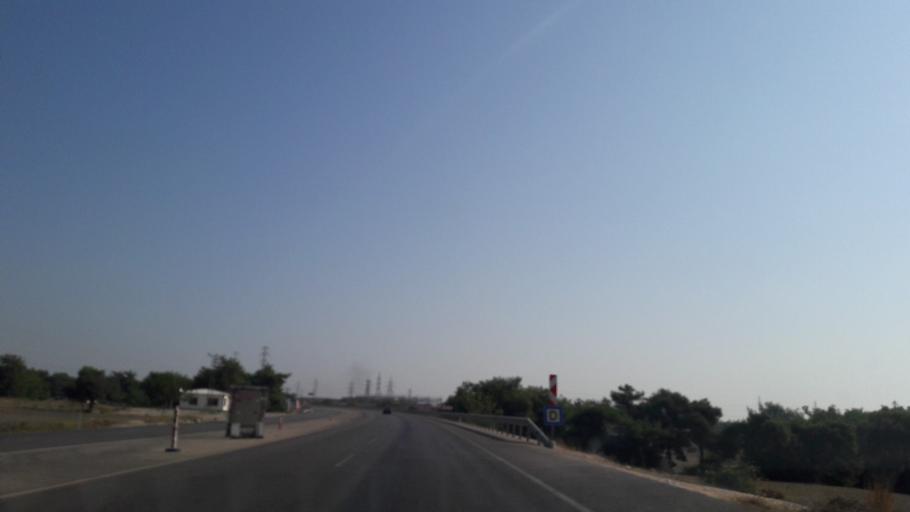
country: TR
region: Adana
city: Yakapinar
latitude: 37.0956
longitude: 35.5010
